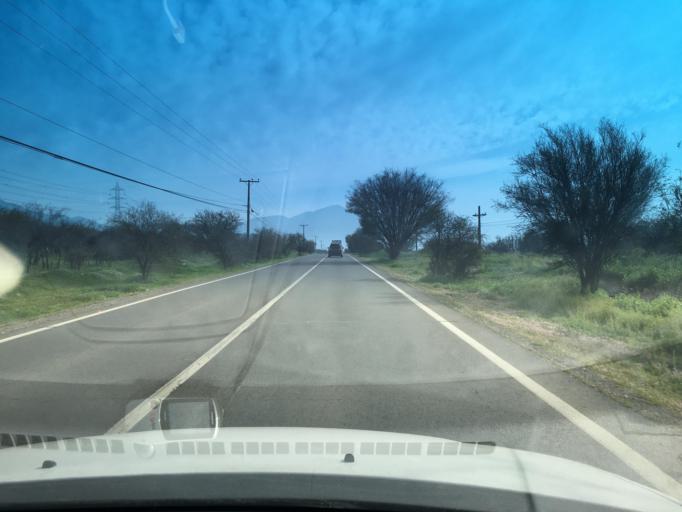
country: CL
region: Santiago Metropolitan
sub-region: Provincia de Chacabuco
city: Lampa
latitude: -33.1378
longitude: -70.9178
